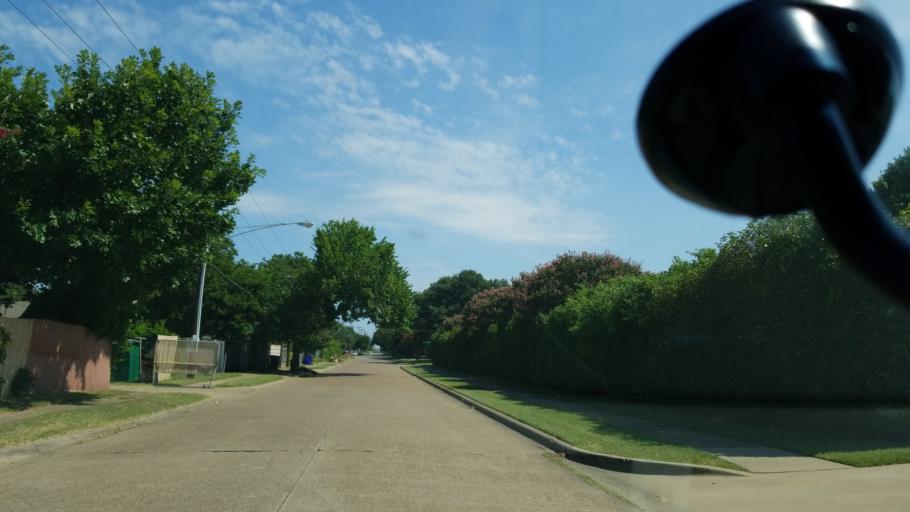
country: US
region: Texas
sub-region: Dallas County
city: Cockrell Hill
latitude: 32.7098
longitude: -96.8762
